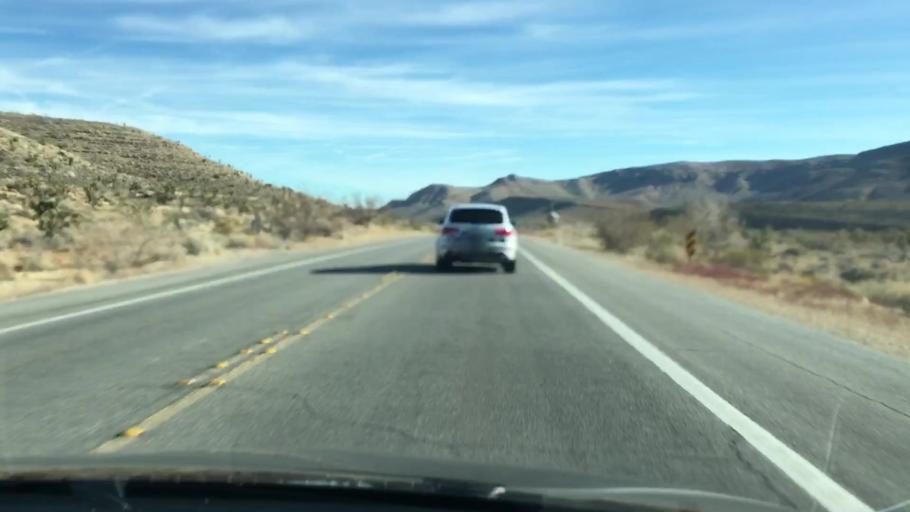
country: US
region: Nevada
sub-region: Clark County
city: Summerlin South
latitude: 36.0686
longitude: -115.4376
